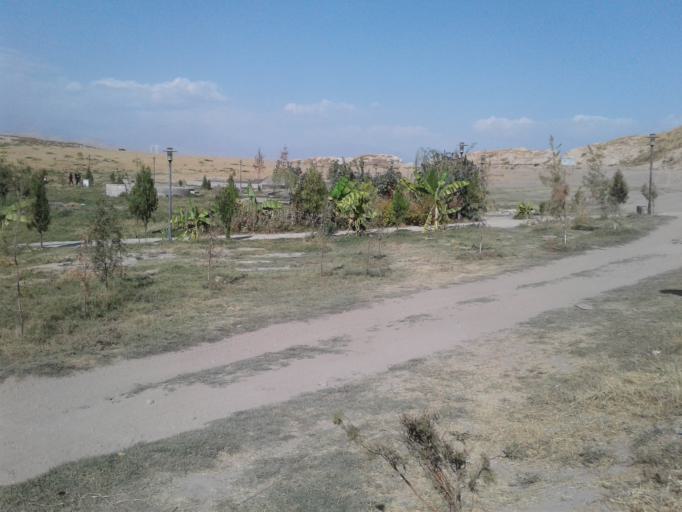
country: TJ
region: Republican Subordination
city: Hisor
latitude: 38.4843
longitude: 68.5916
